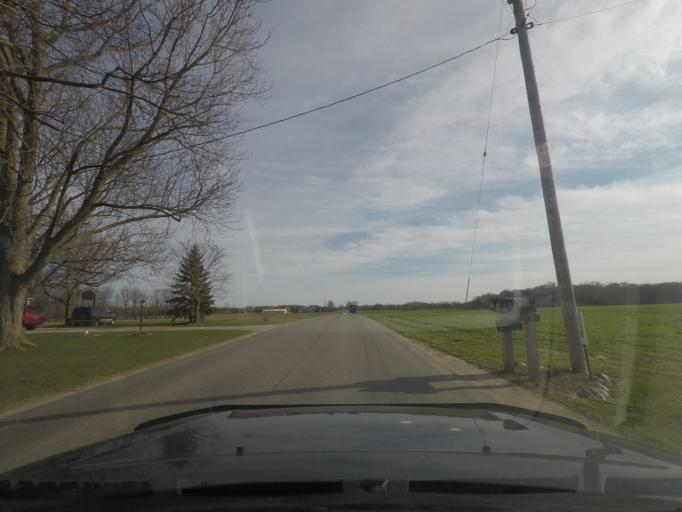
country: US
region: Indiana
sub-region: Elkhart County
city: Dunlap
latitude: 41.5621
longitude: -85.9249
